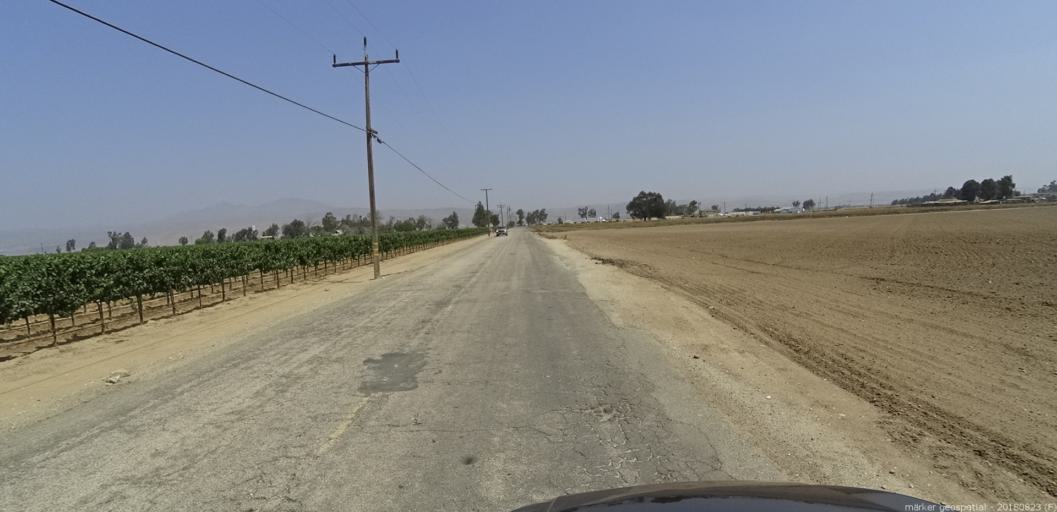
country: US
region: California
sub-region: Monterey County
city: Greenfield
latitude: 36.3340
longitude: -121.2592
